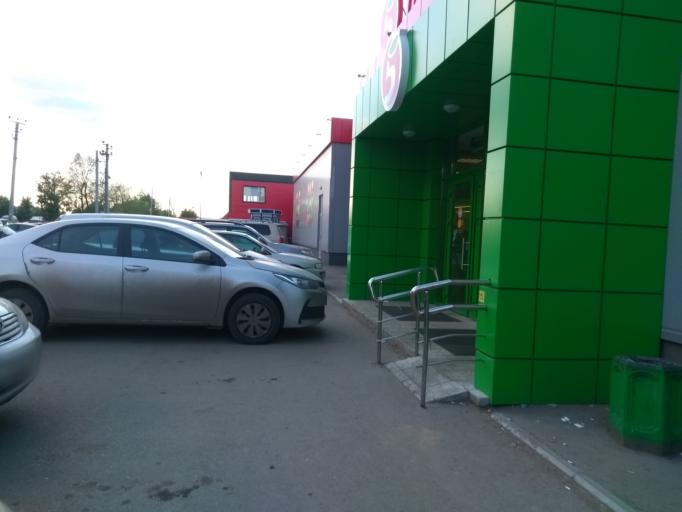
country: RU
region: Perm
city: Perm
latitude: 58.0073
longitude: 56.3255
